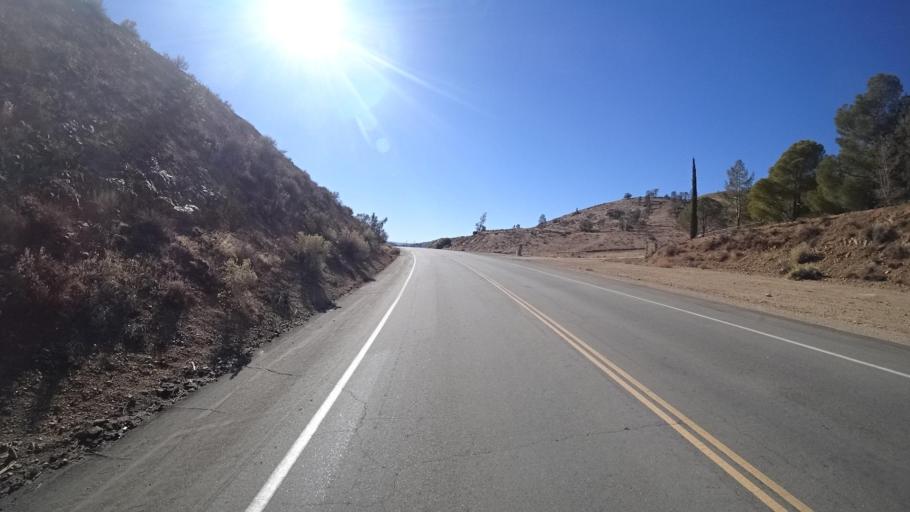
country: US
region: California
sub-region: Kern County
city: Wofford Heights
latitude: 35.7195
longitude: -118.4374
